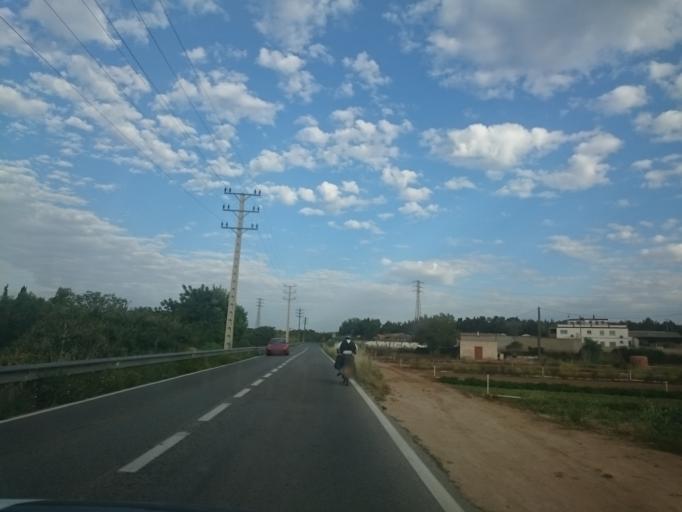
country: ES
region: Catalonia
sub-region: Provincia de Barcelona
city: Vilanova i la Geltru
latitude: 41.2298
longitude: 1.6965
